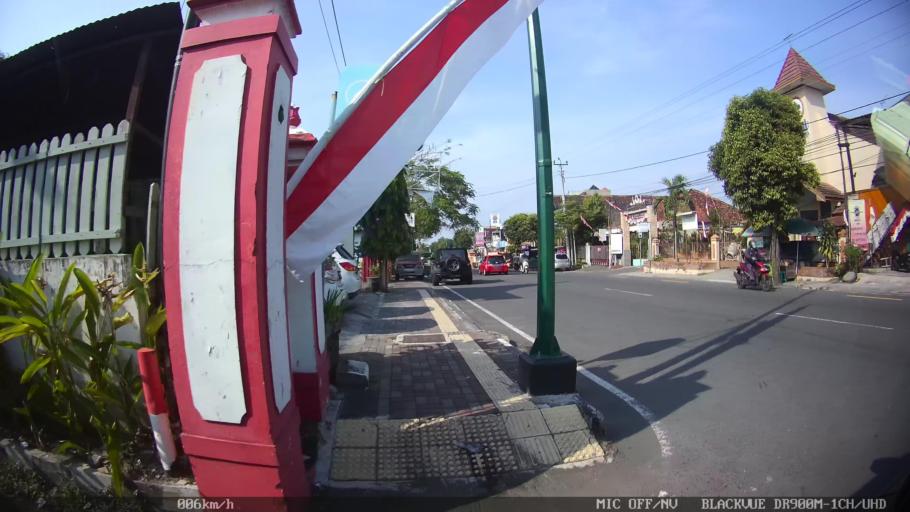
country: ID
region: Daerah Istimewa Yogyakarta
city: Yogyakarta
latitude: -7.7871
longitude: 110.3577
